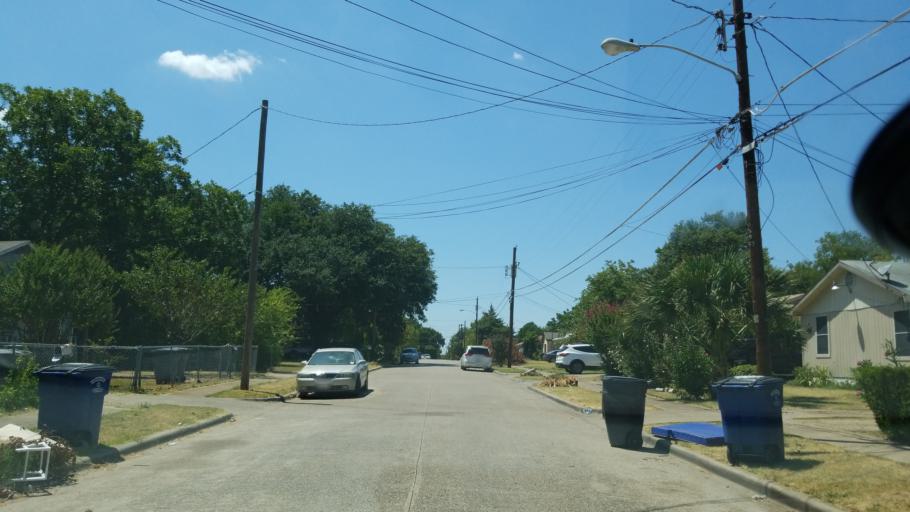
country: US
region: Texas
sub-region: Dallas County
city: Cockrell Hill
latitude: 32.7274
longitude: -96.8862
